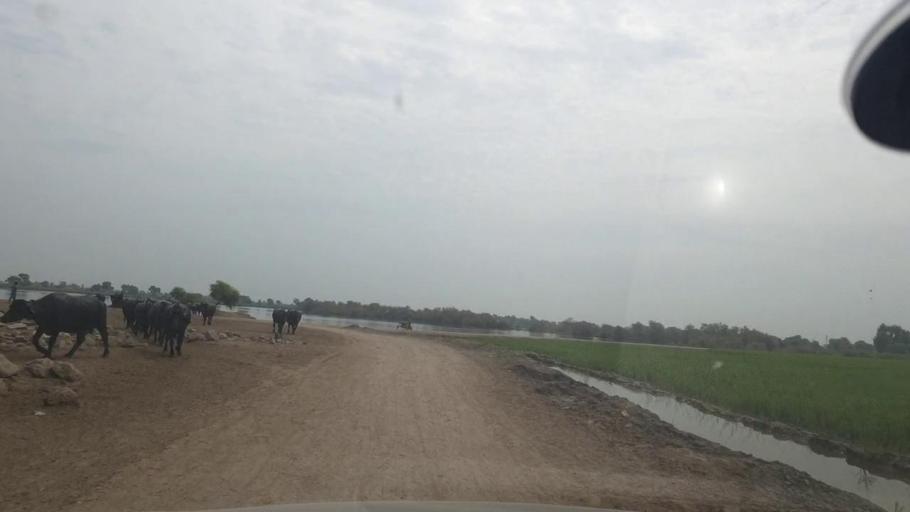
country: PK
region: Sindh
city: Jacobabad
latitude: 28.2410
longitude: 68.5407
